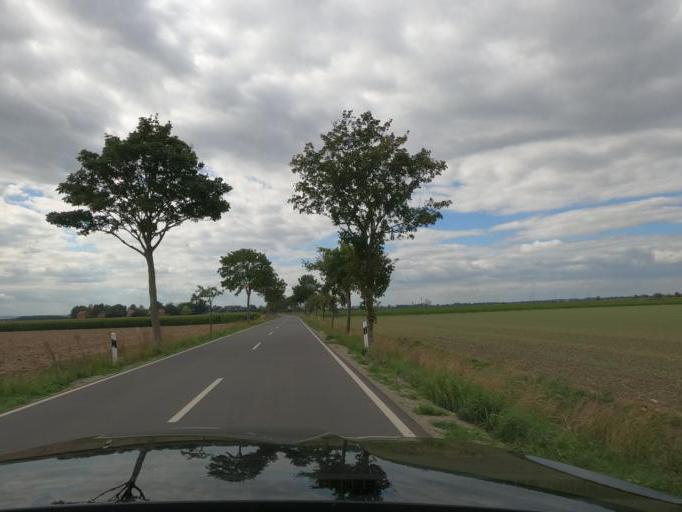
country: DE
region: Lower Saxony
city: Schellerten
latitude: 52.2278
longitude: 10.0969
